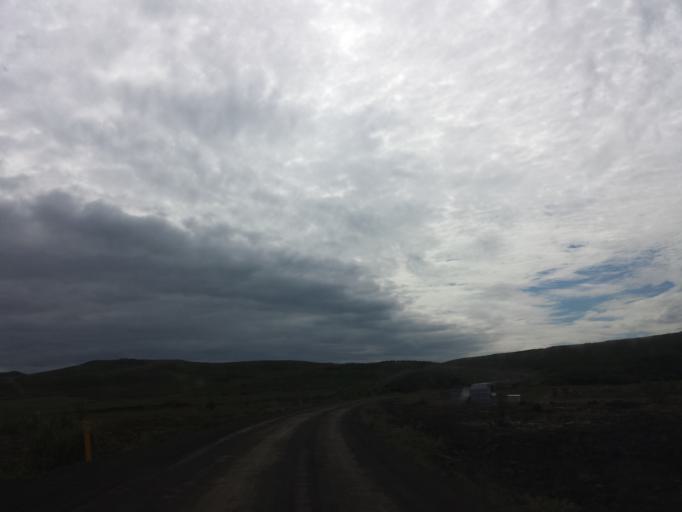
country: IS
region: Northeast
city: Husavik
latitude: 65.9329
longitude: -17.4445
